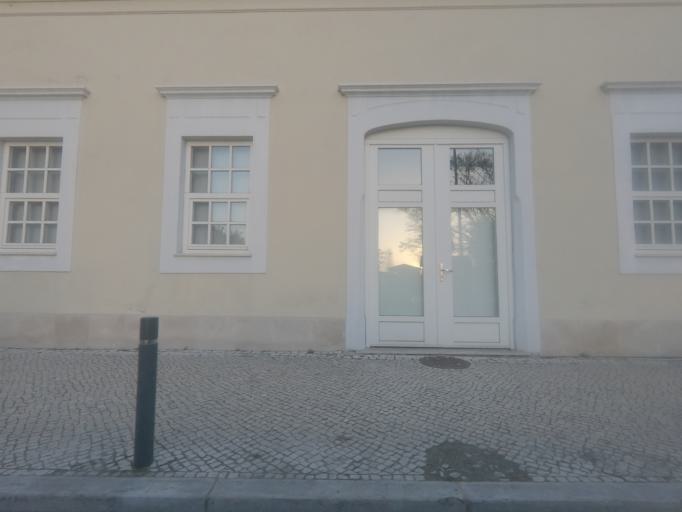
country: PT
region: Leiria
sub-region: Marinha Grande
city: Marinha Grande
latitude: 39.7489
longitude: -8.9329
